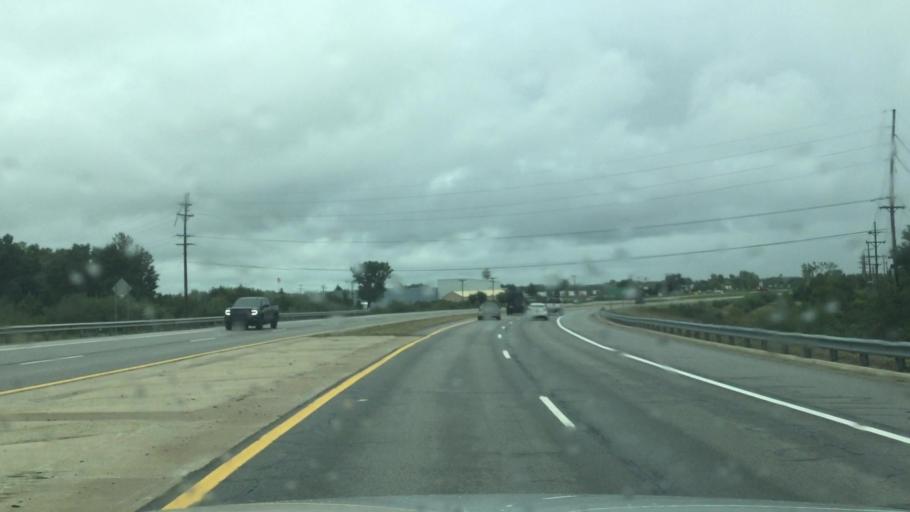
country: US
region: Michigan
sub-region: Livingston County
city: Howell
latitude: 42.6216
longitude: -83.9848
